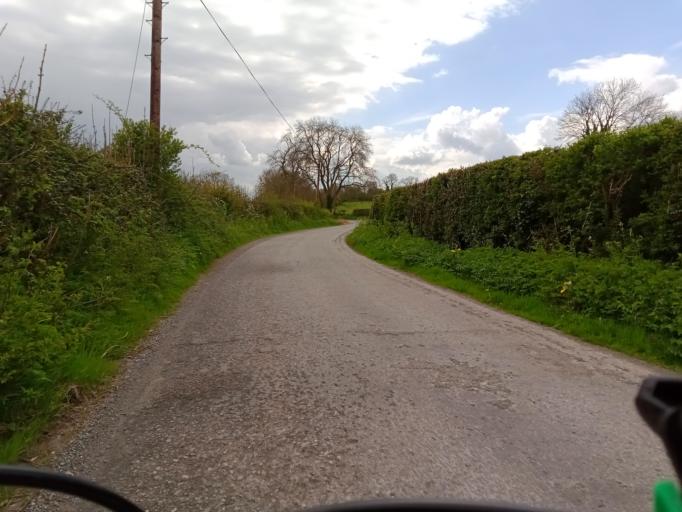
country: IE
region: Leinster
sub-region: Kilkenny
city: Kilkenny
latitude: 52.6344
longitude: -7.2811
